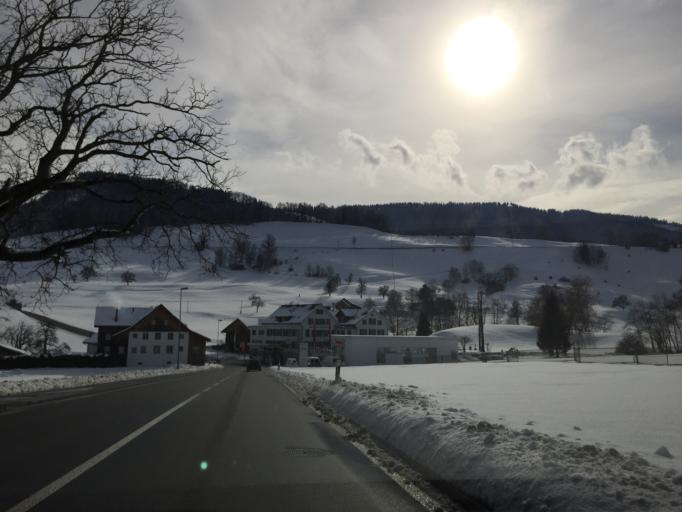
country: CH
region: Zurich
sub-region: Bezirk Horgen
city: Richterswil
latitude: 47.1861
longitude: 8.6835
